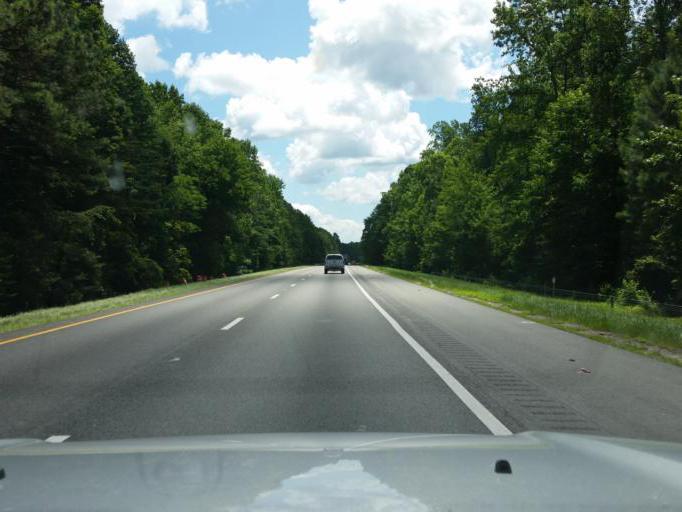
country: US
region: Virginia
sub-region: King William County
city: West Point
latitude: 37.4152
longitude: -76.8056
